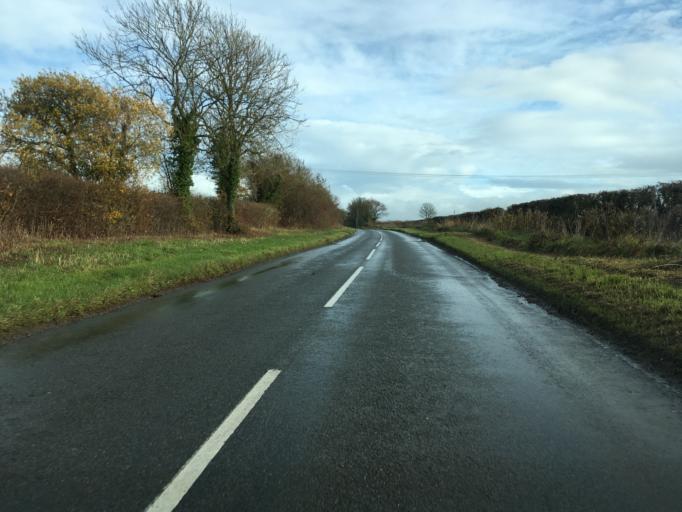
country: GB
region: England
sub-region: South Gloucestershire
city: Pucklechurch
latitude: 51.4892
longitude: -2.4134
